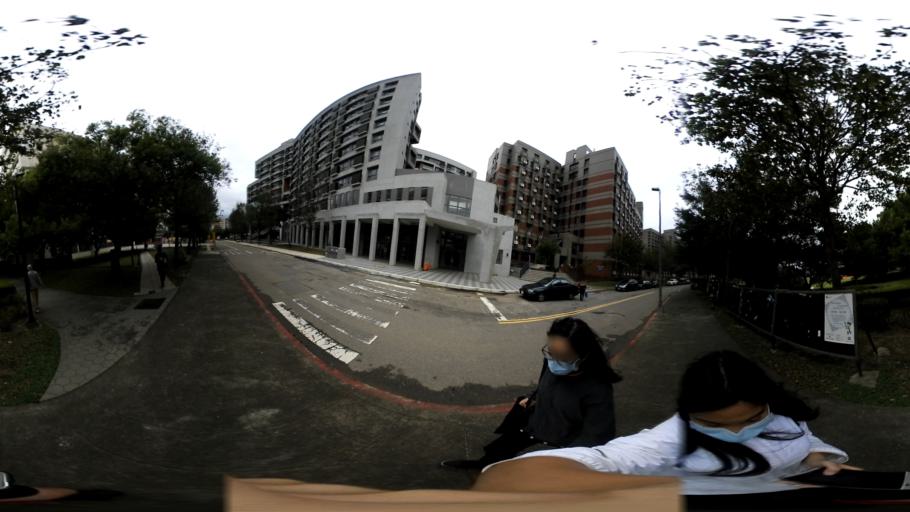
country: TW
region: Taiwan
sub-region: Hsinchu
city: Hsinchu
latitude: 24.7840
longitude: 120.9968
